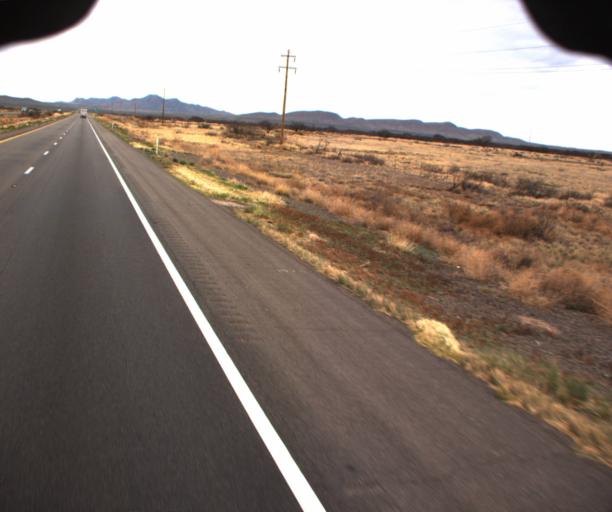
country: US
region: Arizona
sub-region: Cochise County
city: Willcox
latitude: 32.1923
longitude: -109.9232
